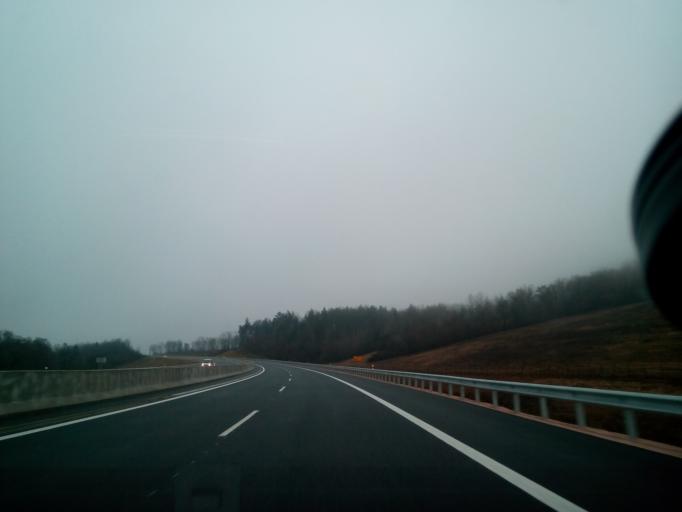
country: SK
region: Presovsky
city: Sabinov
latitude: 49.0130
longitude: 21.0417
